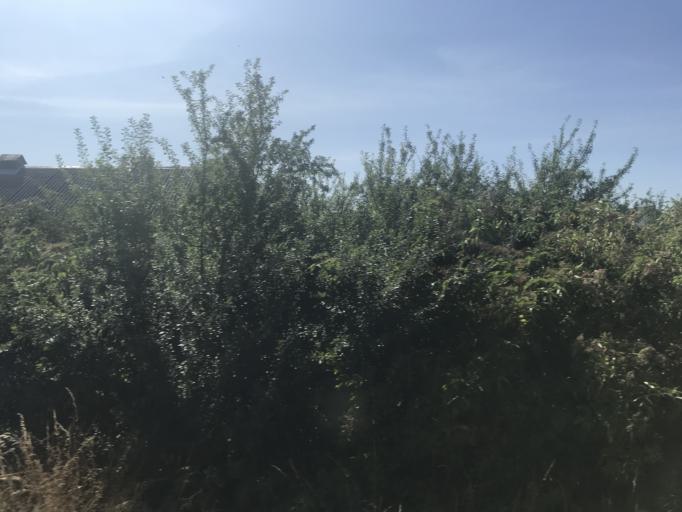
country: PL
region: West Pomeranian Voivodeship
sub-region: Powiat policki
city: Przeclaw
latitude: 53.3816
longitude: 14.4686
